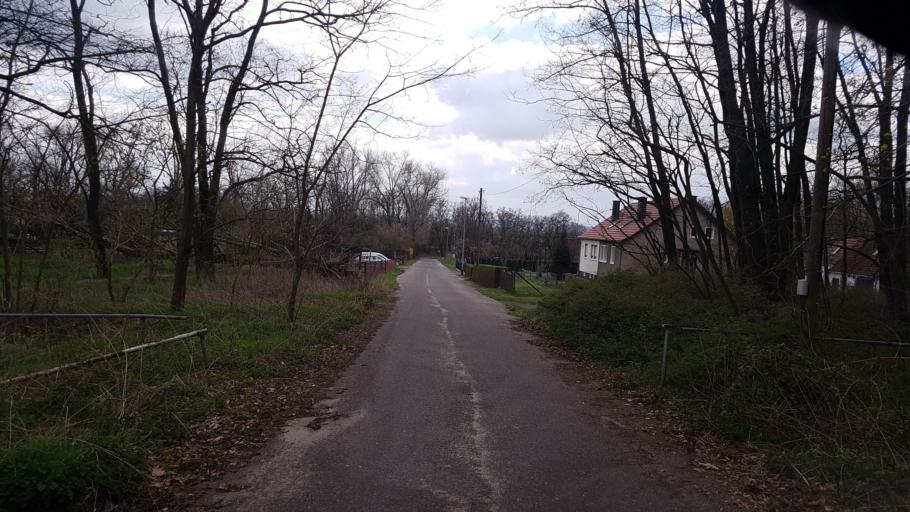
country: DE
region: Brandenburg
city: Plessa
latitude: 51.4729
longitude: 13.6072
